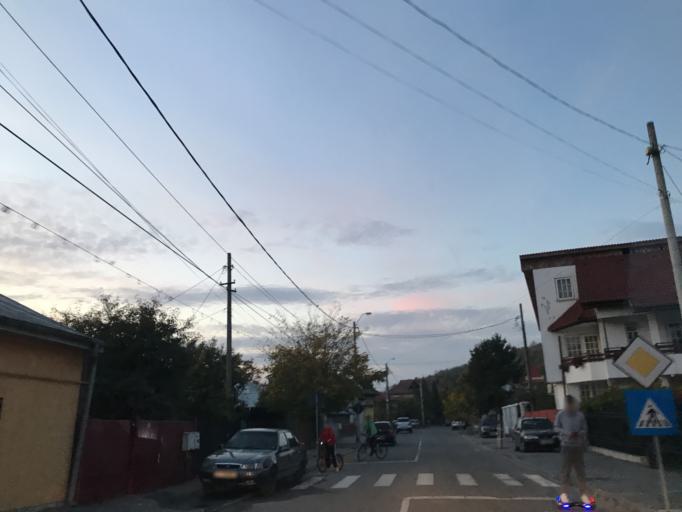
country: RO
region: Olt
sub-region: Municipiul Slatina
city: Slatina
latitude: 44.4329
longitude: 24.3546
